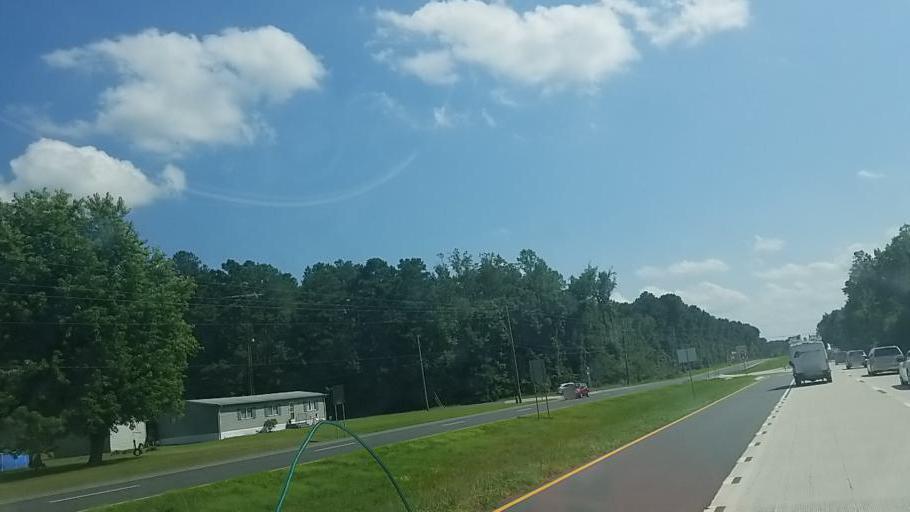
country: US
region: Delaware
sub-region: Sussex County
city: Milford
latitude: 38.8279
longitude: -75.4390
